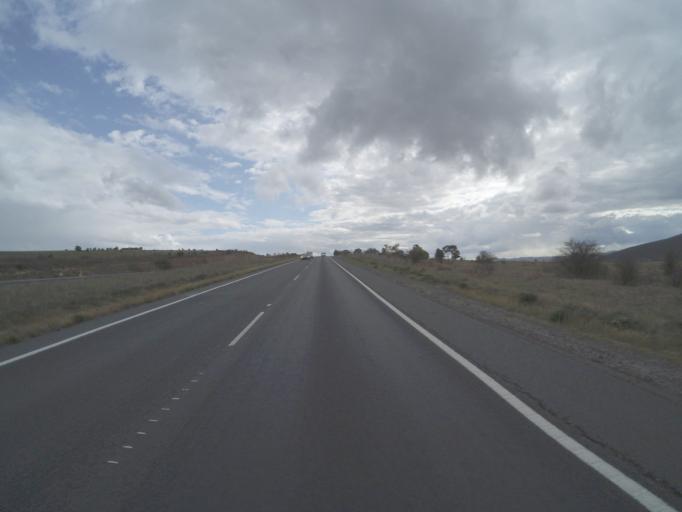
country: AU
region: New South Wales
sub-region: Goulburn Mulwaree
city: Goulburn
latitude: -34.7337
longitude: 149.8003
